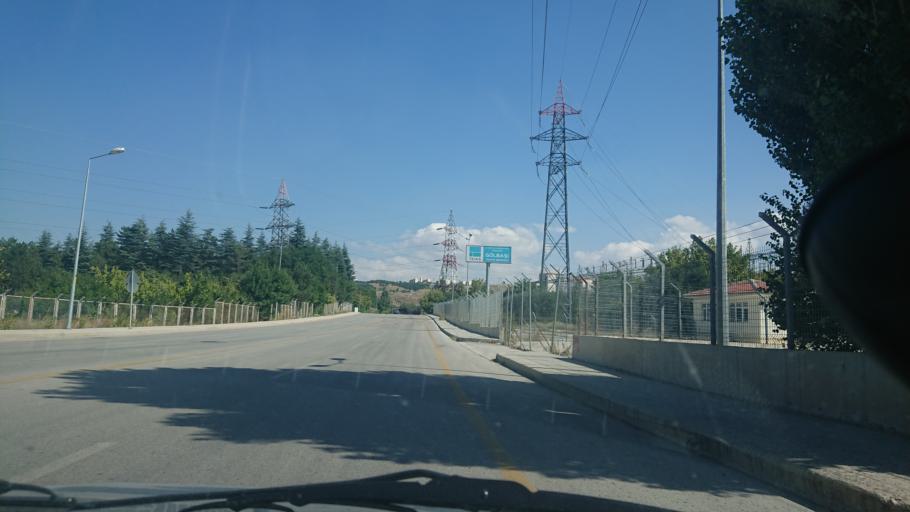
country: TR
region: Ankara
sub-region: Goelbasi
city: Golbasi
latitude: 39.8074
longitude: 32.8166
